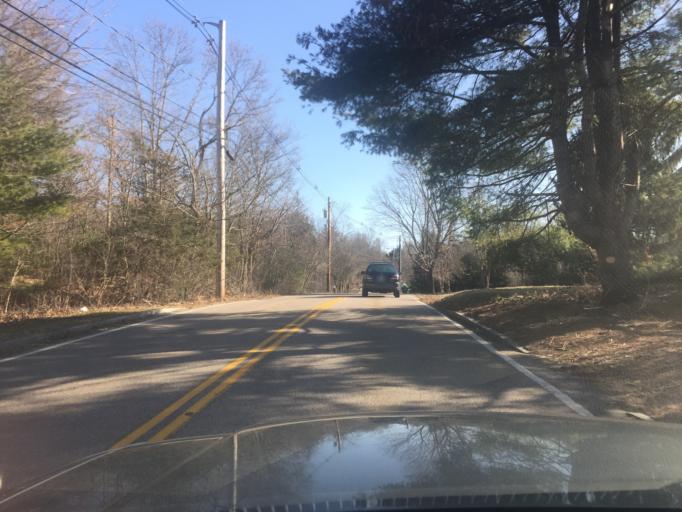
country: US
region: Massachusetts
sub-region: Norfolk County
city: Millis-Clicquot
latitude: 42.1377
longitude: -71.3586
